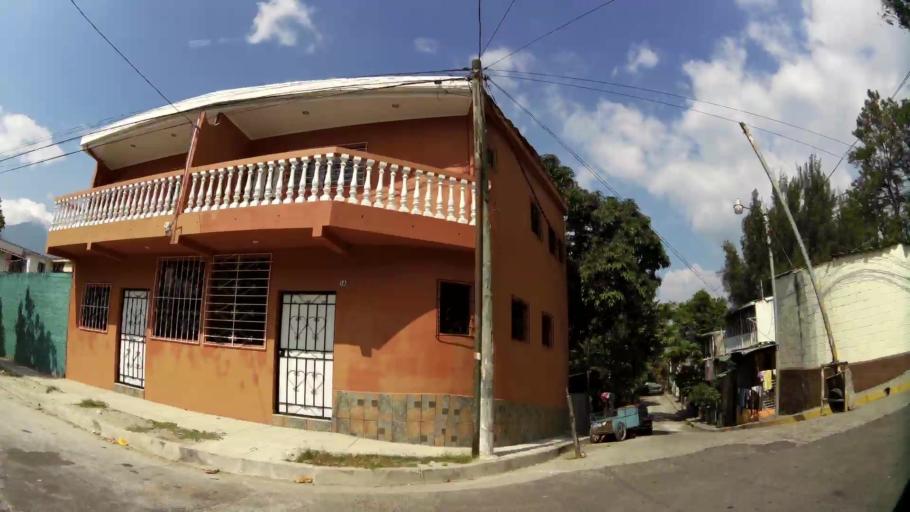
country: SV
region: San Salvador
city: Mejicanos
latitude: 13.7189
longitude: -89.2071
